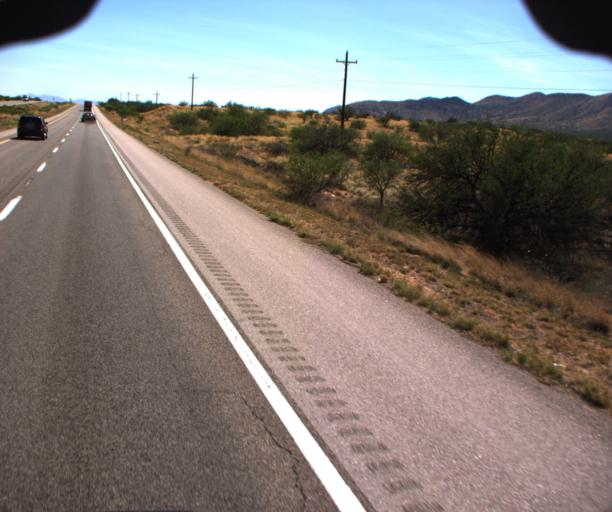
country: US
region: Arizona
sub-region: Cochise County
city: Whetstone
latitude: 31.8877
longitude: -110.3414
